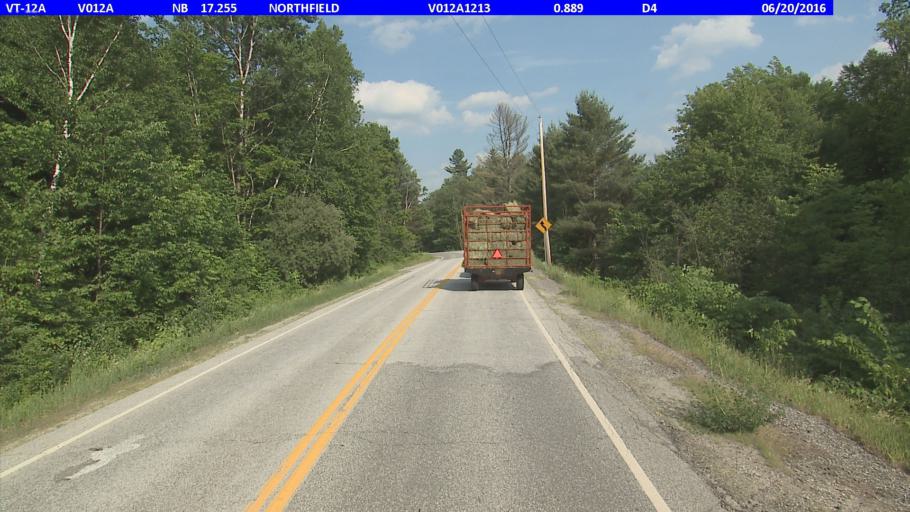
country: US
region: Vermont
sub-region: Washington County
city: Northfield
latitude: 44.1171
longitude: -72.7092
